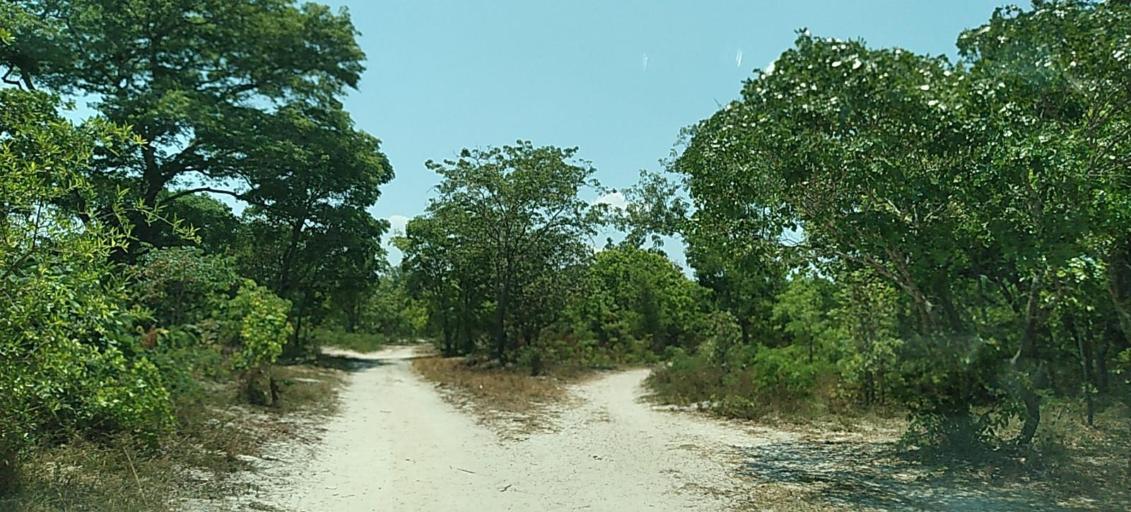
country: ZM
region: Central
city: Kapiri Mposhi
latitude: -13.6713
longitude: 28.5019
